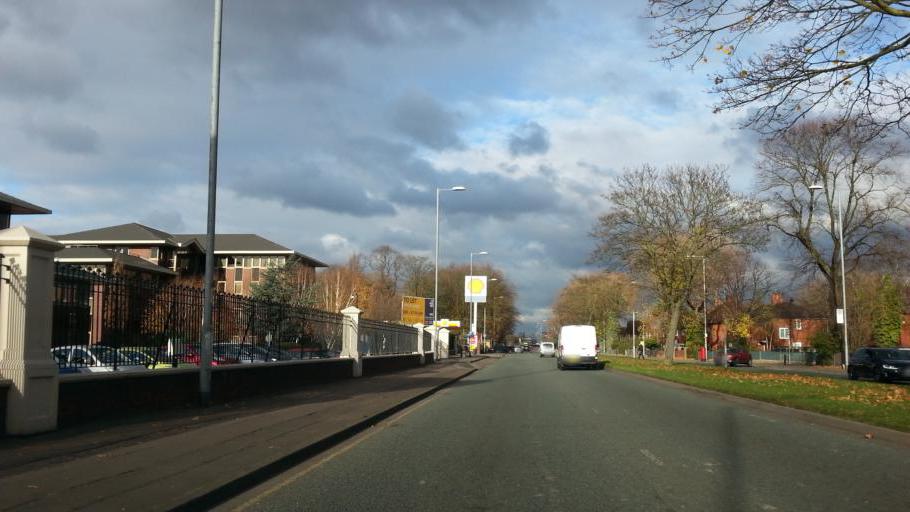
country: GB
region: England
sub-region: Manchester
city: Hulme
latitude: 53.4476
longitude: -2.2447
